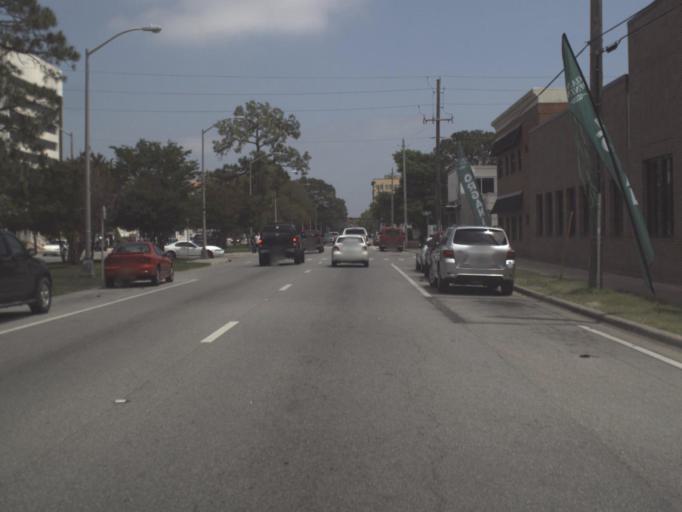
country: US
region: Florida
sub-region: Escambia County
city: Pensacola
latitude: 30.4118
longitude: -87.2212
